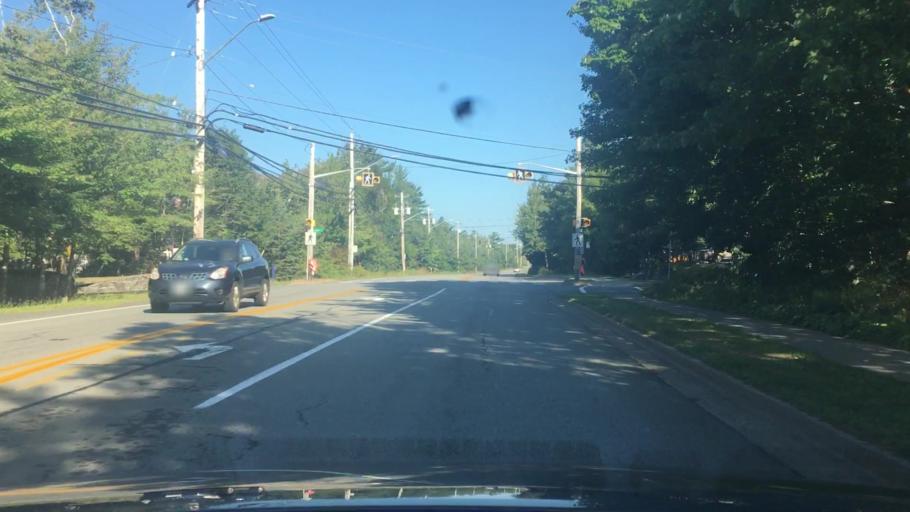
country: CA
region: Nova Scotia
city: Dartmouth
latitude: 44.7184
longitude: -63.6851
